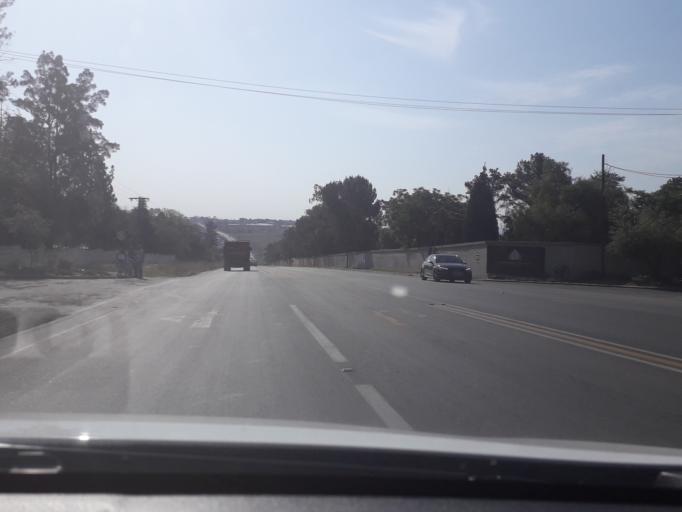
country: ZA
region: Gauteng
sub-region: City of Johannesburg Metropolitan Municipality
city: Diepsloot
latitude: -25.9813
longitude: 27.9717
